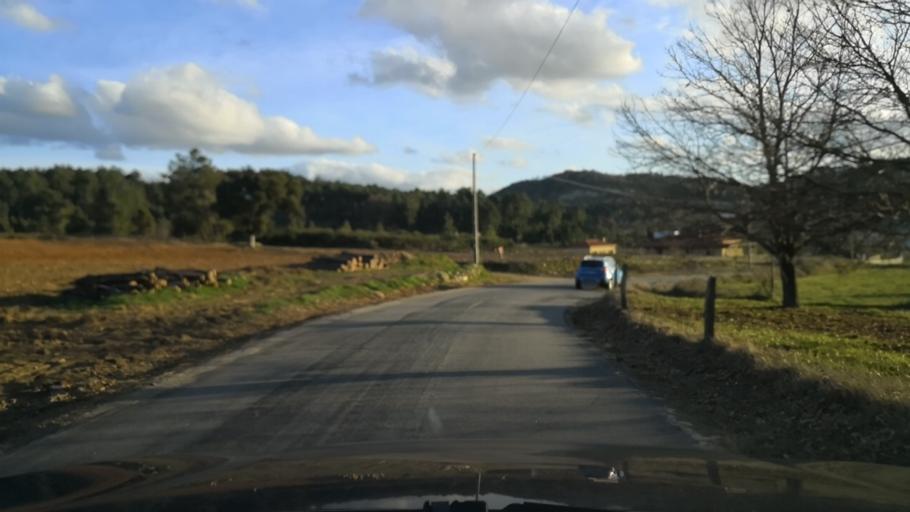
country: PT
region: Braganca
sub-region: Carrazeda de Ansiaes
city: Carrazeda de Anciaes
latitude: 41.2262
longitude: -7.3385
